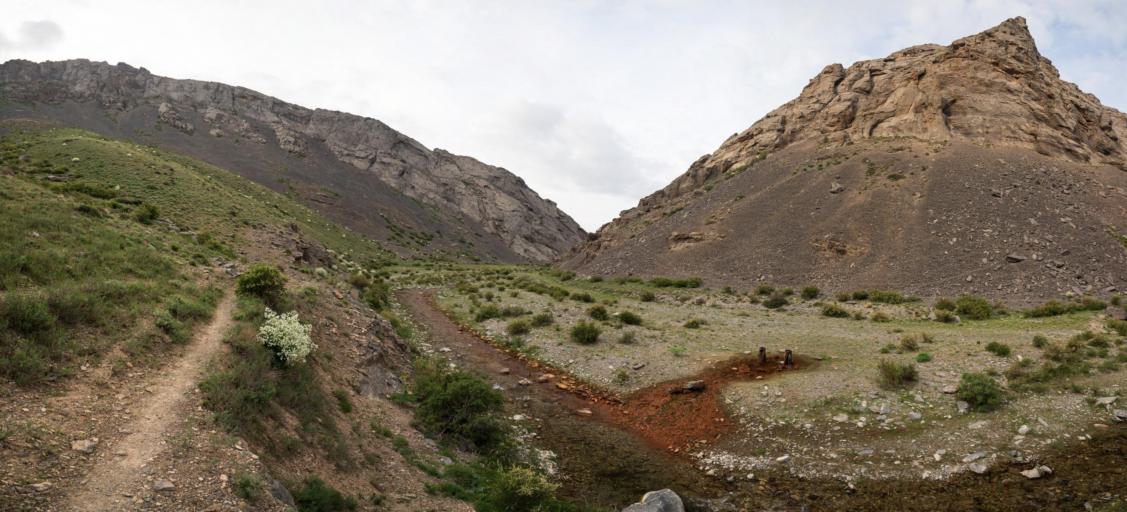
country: KZ
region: Ongtustik Qazaqstan
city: Ashchysay
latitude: 43.5844
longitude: 68.9003
